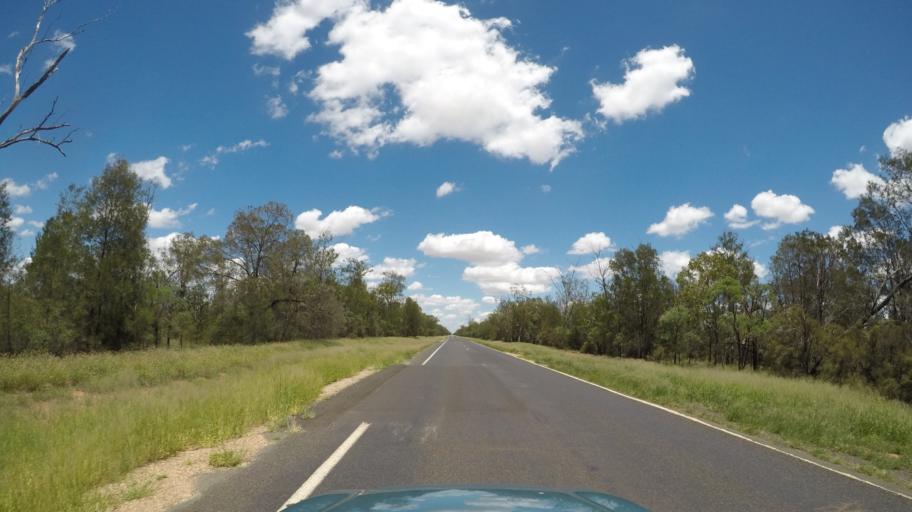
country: AU
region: Queensland
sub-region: Goondiwindi
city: Goondiwindi
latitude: -28.1597
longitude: 150.6337
